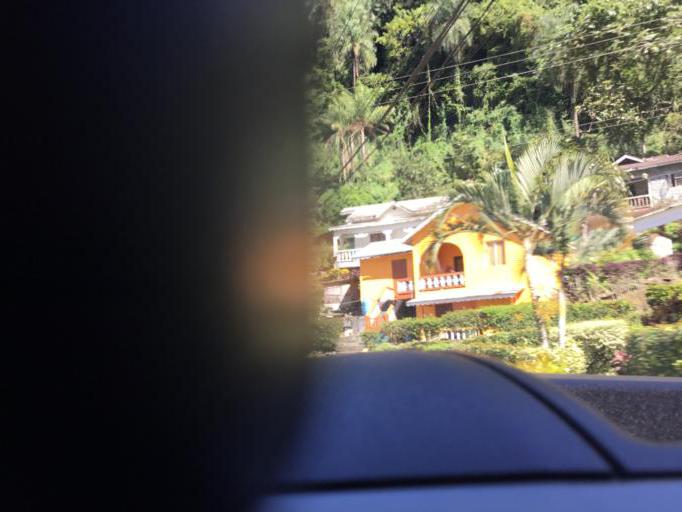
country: VC
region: Saint David
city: Chateaubelair
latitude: 13.2588
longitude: -61.2498
